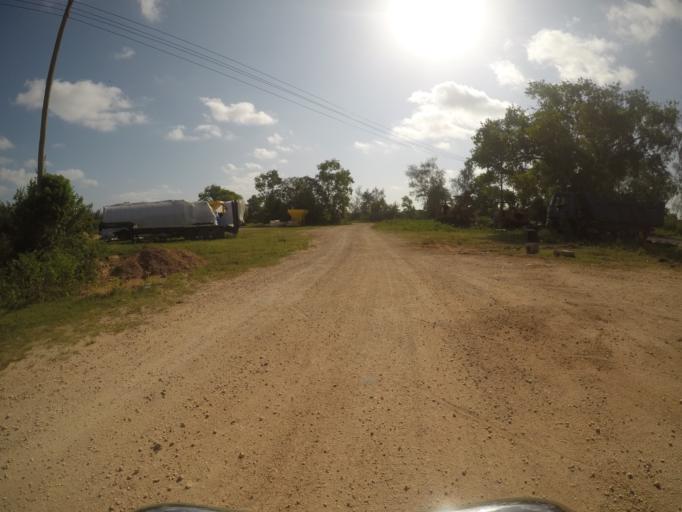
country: TZ
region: Zanzibar Central/South
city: Koani
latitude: -6.2163
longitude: 39.3334
